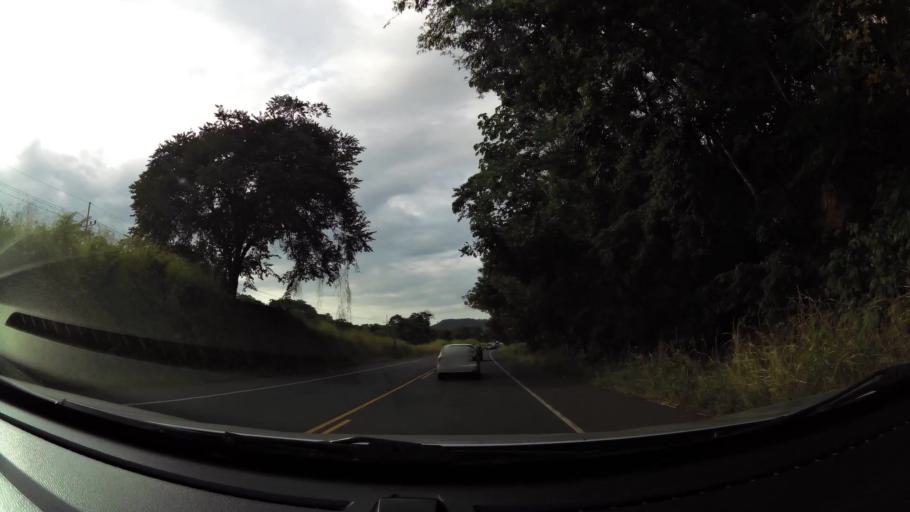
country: CR
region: Puntarenas
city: Esparza
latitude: 9.8973
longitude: -84.6561
